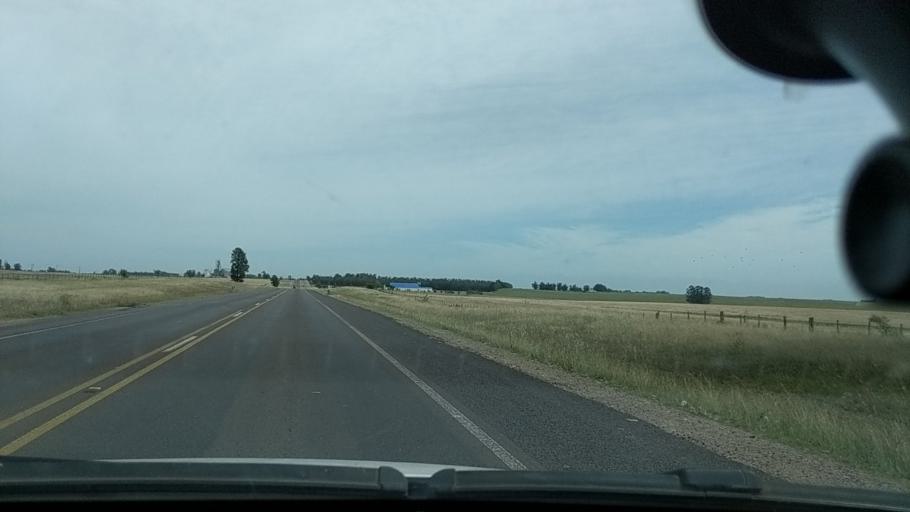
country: UY
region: Durazno
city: Durazno
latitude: -33.4605
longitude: -56.4636
